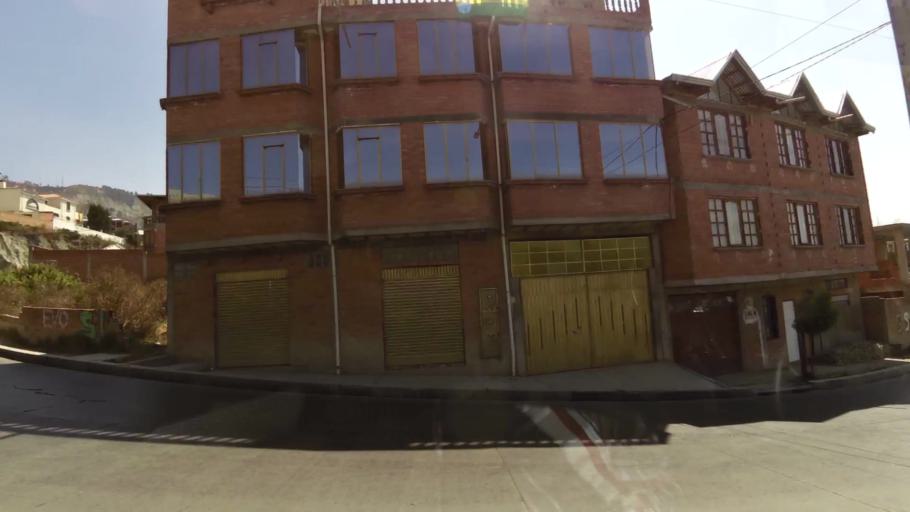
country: BO
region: La Paz
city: La Paz
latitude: -16.5322
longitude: -68.1269
